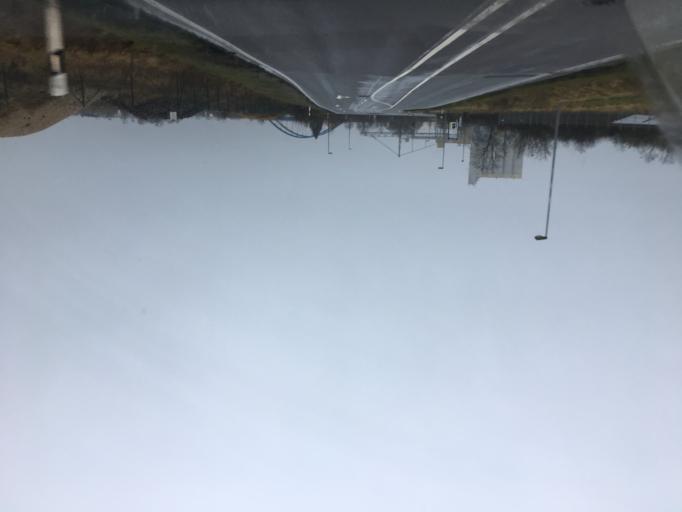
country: DE
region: Saxony-Anhalt
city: Gross Ammensleben
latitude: 52.2484
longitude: 11.5027
